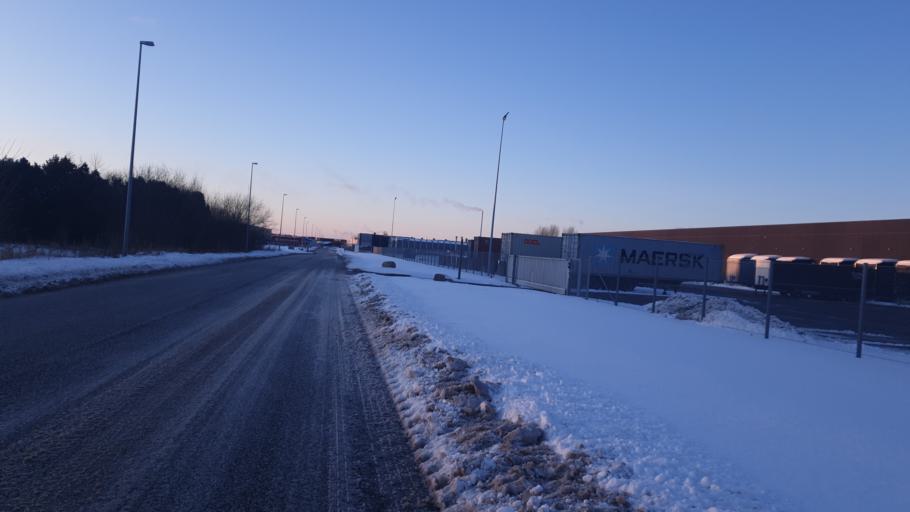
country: DK
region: Central Jutland
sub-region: Hedensted Kommune
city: Hedensted
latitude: 55.7883
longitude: 9.6825
